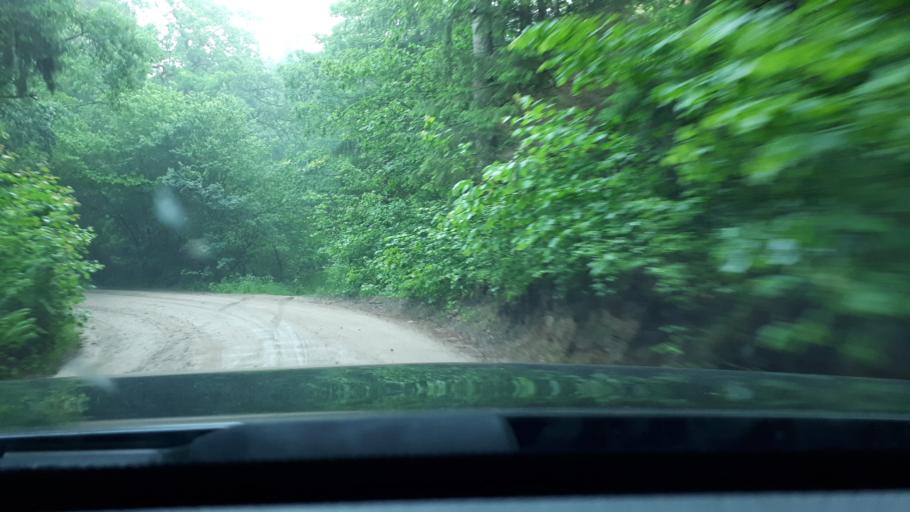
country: PL
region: Podlasie
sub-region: Powiat bialostocki
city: Suprasl
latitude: 53.2265
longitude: 23.3510
